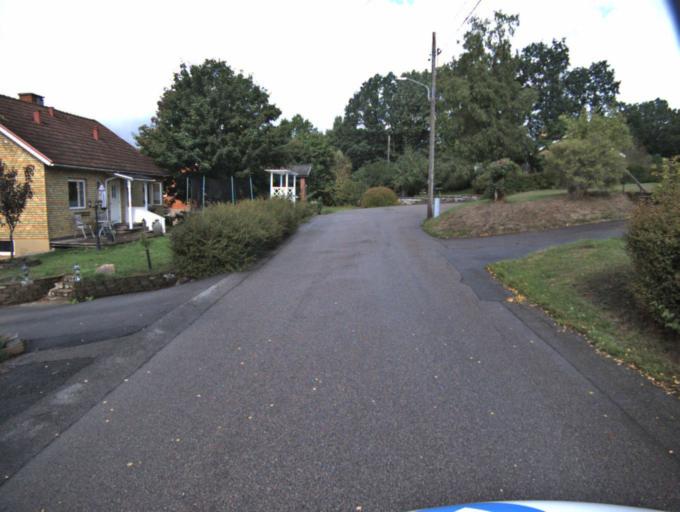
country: SE
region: Vaestra Goetaland
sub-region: Ulricehamns Kommun
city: Ulricehamn
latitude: 57.7214
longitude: 13.3053
